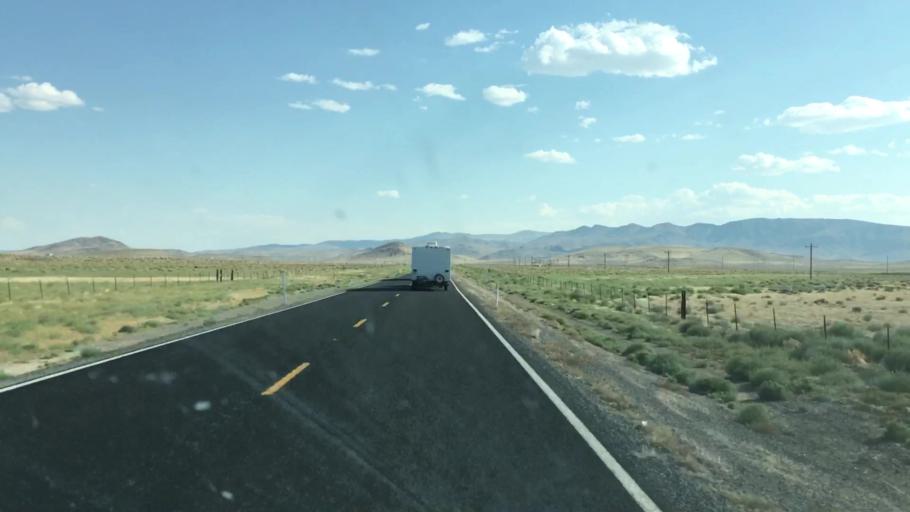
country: US
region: Nevada
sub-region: Lyon County
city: Fernley
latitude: 39.6623
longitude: -119.3319
